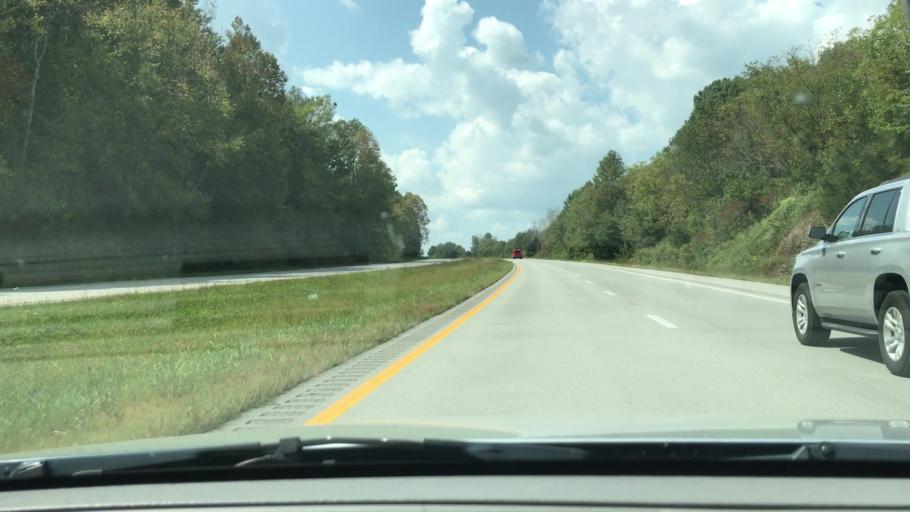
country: US
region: Kentucky
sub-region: Casey County
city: Liberty
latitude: 37.1008
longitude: -84.8513
